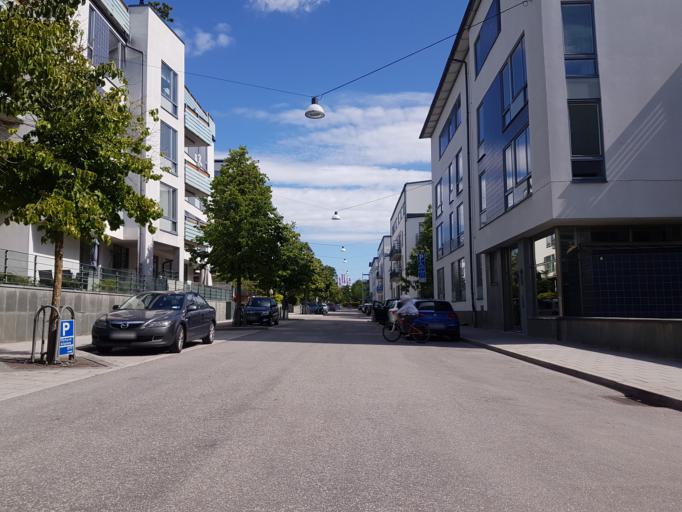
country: SE
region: Stockholm
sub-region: Stockholms Kommun
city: OEstermalm
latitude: 59.3039
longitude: 18.1077
